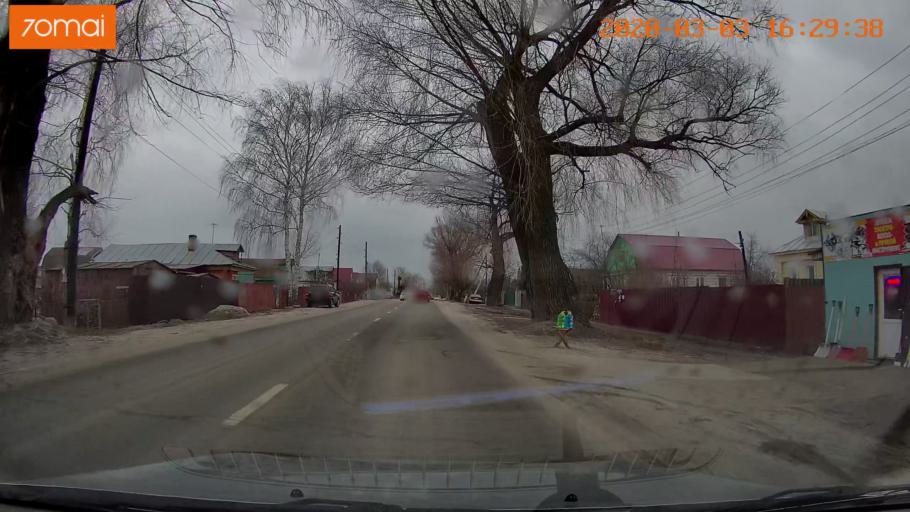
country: RU
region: Moskovskaya
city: Konobeyevo
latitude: 55.4364
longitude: 38.7025
